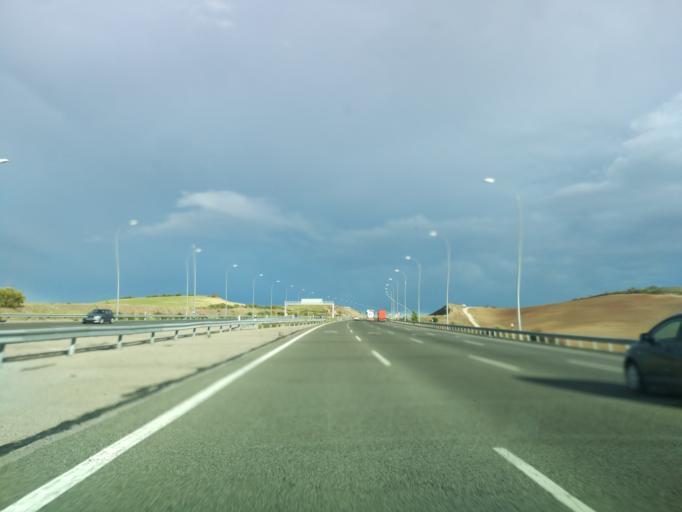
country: ES
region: Madrid
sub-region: Provincia de Madrid
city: Paracuellos de Jarama
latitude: 40.5386
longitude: -3.5300
